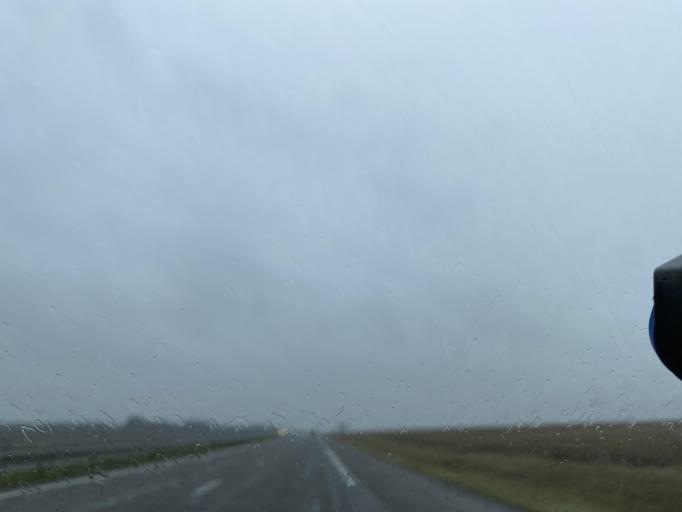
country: FR
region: Centre
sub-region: Departement d'Eure-et-Loir
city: Villemeux-sur-Eure
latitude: 48.6178
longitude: 1.4173
